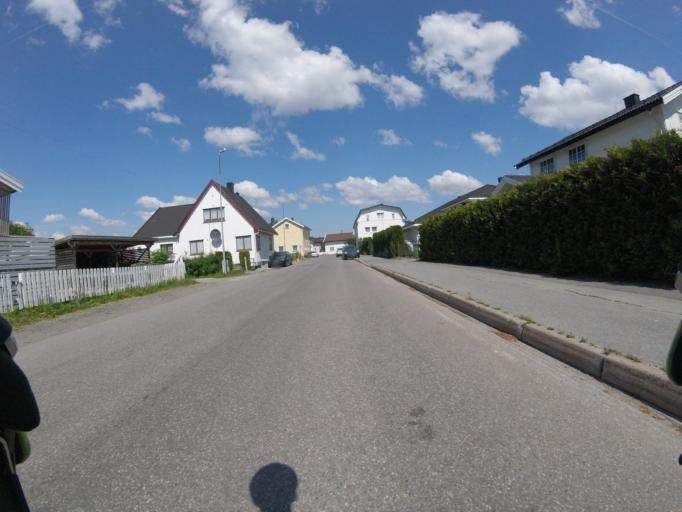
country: NO
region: Akershus
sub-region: Skedsmo
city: Lillestrom
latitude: 59.9508
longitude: 11.0605
